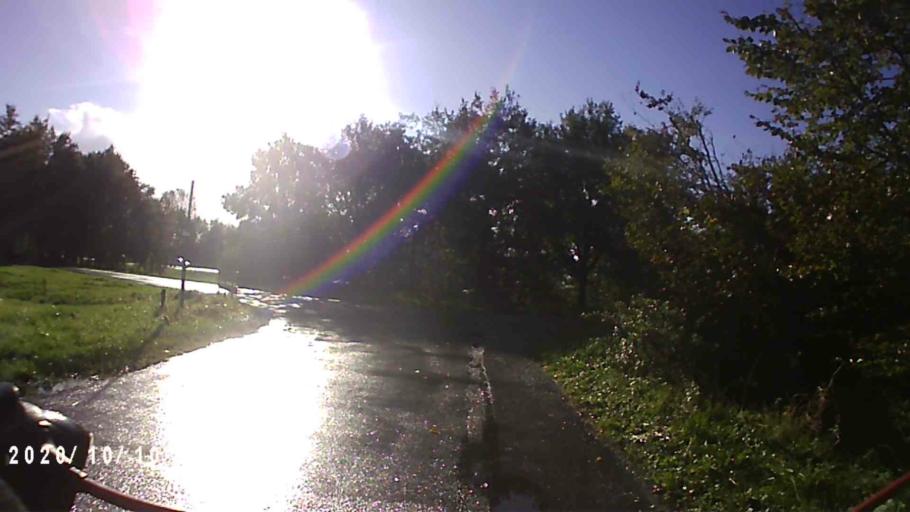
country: NL
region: Friesland
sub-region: Gemeente Achtkarspelen
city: Surhuisterveen
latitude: 53.1387
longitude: 6.2123
